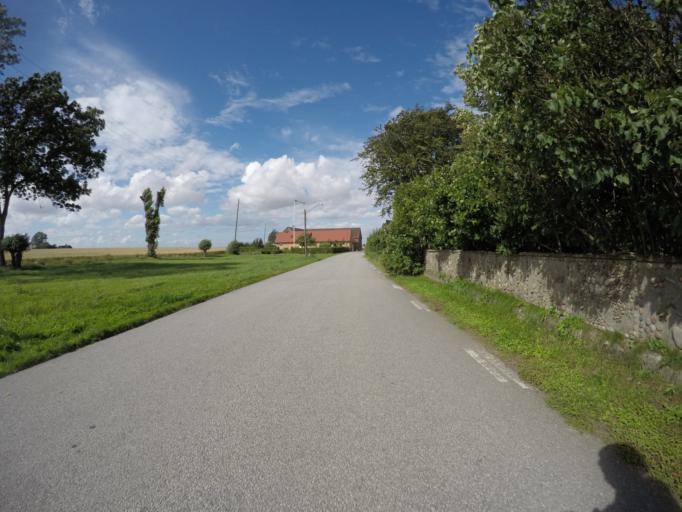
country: SE
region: Skane
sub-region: Simrishamns Kommun
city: Simrishamn
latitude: 55.4978
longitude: 14.2032
